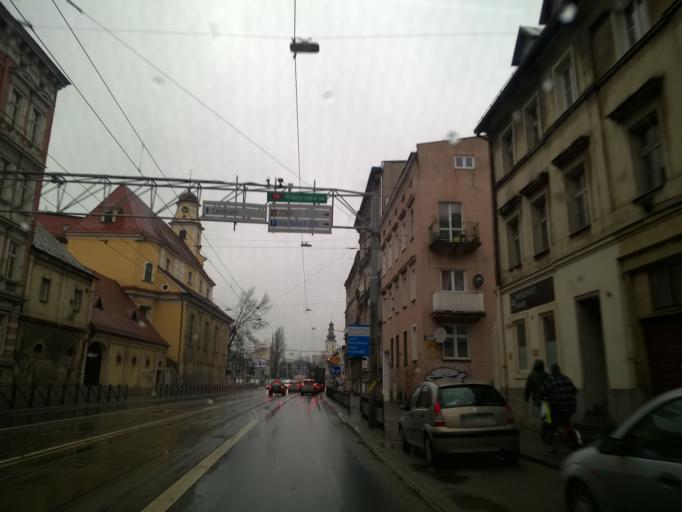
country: PL
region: Lower Silesian Voivodeship
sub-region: Powiat wroclawski
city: Wroclaw
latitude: 51.1035
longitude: 17.0501
